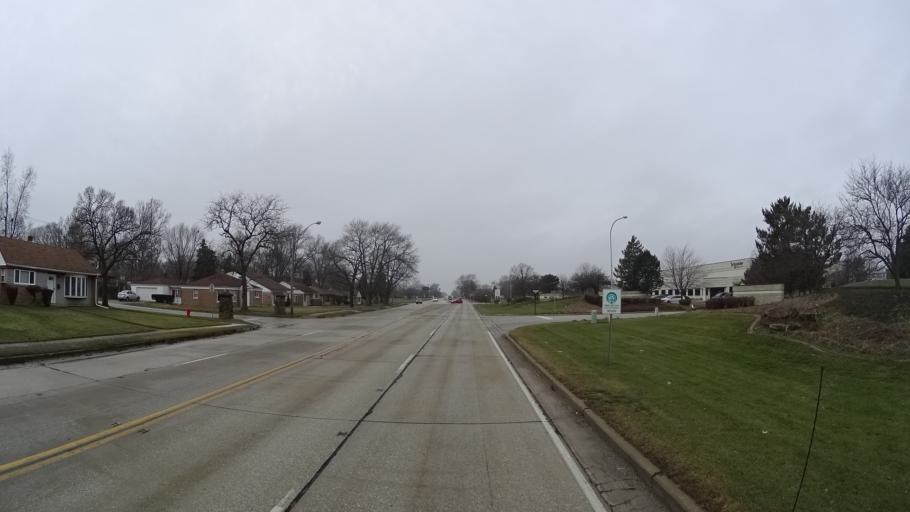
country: US
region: Illinois
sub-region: Cook County
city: Homewood
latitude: 41.5718
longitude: -87.6758
